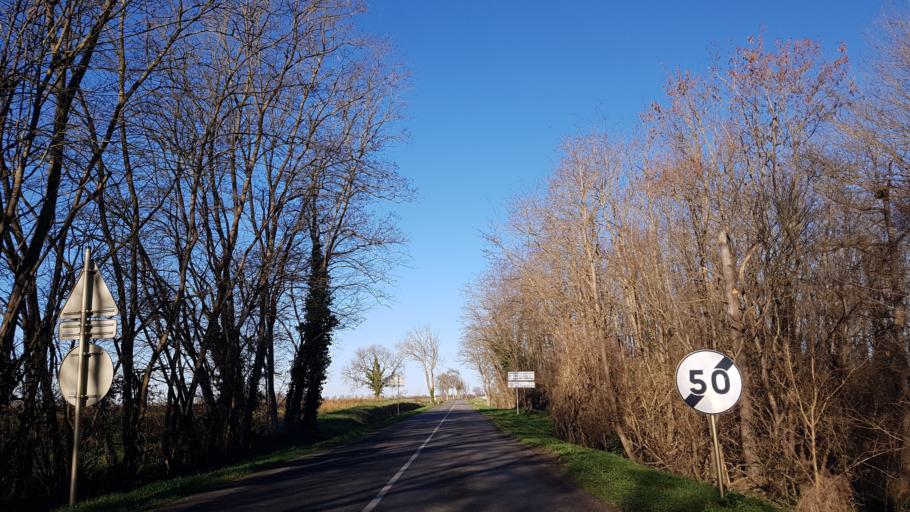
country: FR
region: Midi-Pyrenees
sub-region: Departement de l'Ariege
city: Mazeres
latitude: 43.2674
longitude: 1.6570
